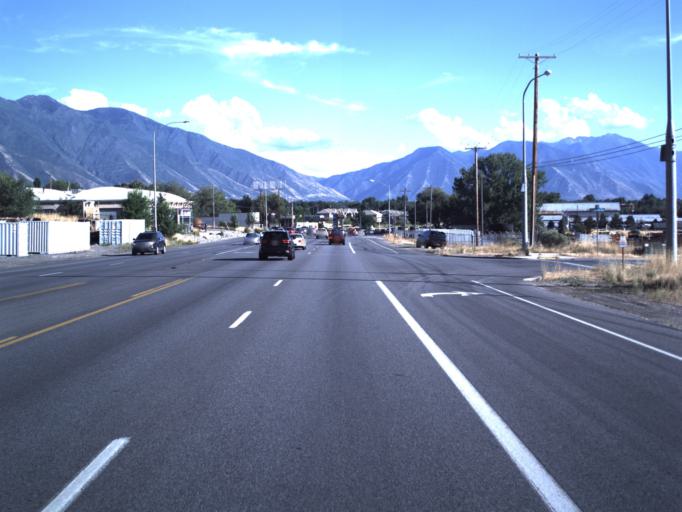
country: US
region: Utah
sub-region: Utah County
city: Springville
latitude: 40.1896
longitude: -111.6115
